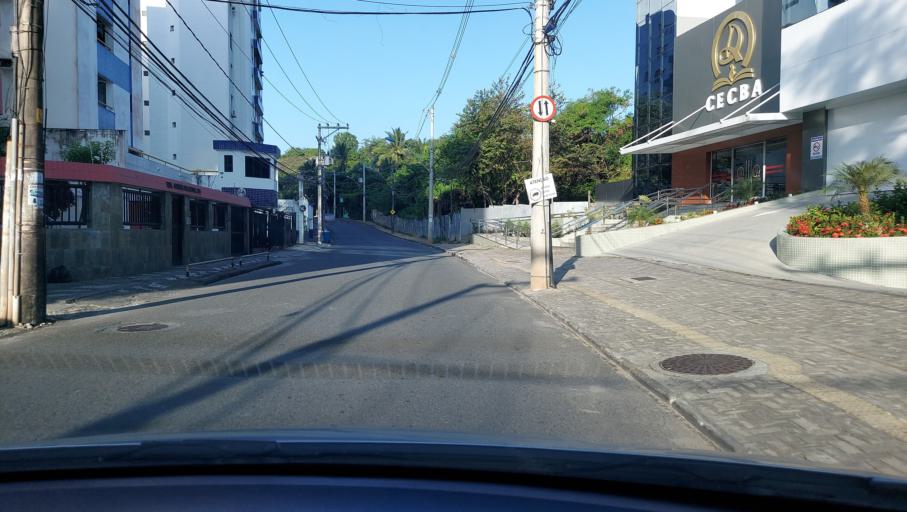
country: BR
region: Bahia
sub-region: Salvador
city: Salvador
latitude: -12.9886
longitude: -38.4460
